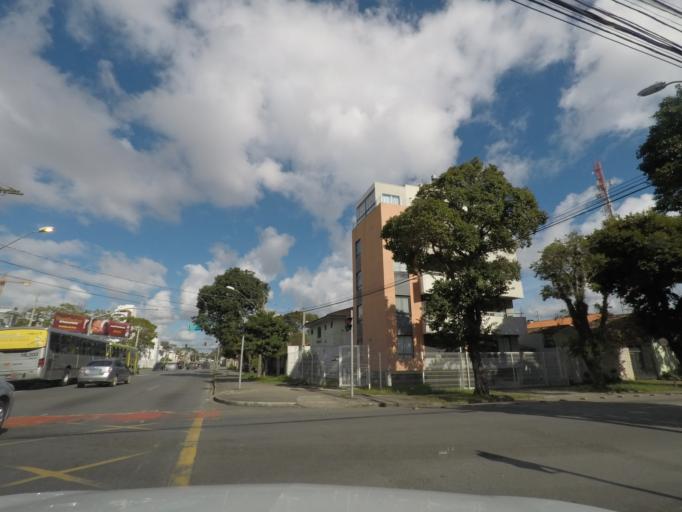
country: BR
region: Parana
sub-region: Curitiba
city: Curitiba
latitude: -25.4460
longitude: -49.2541
